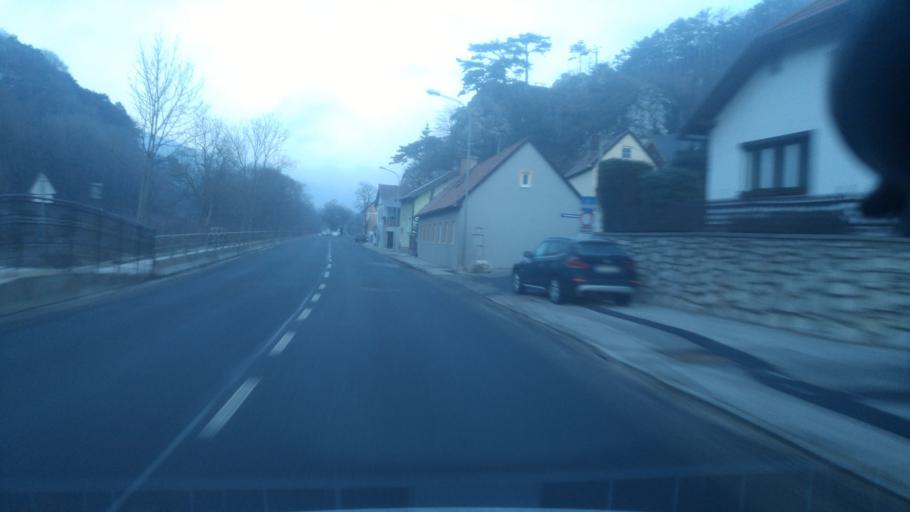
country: AT
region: Lower Austria
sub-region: Politischer Bezirk Baden
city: Pottenstein
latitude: 47.9670
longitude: 16.0859
